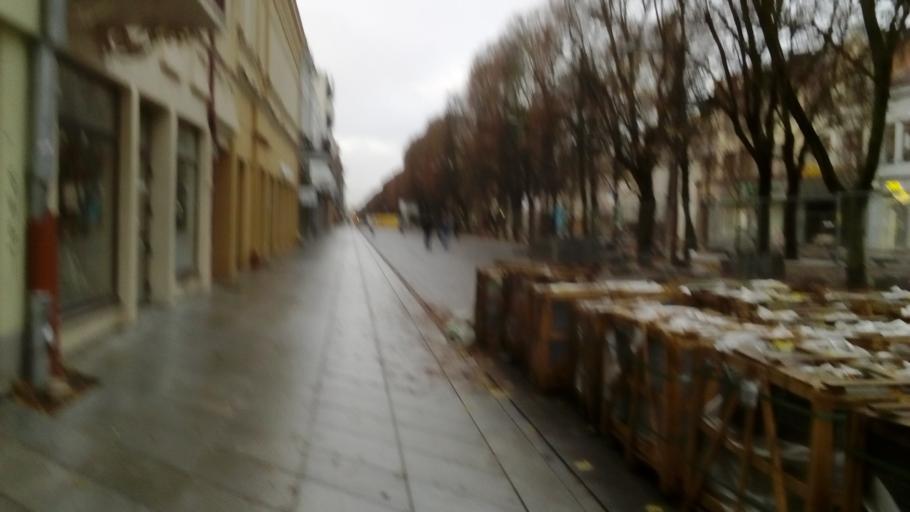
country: LT
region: Kauno apskritis
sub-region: Kaunas
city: Kaunas
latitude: 54.9003
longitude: 23.9182
